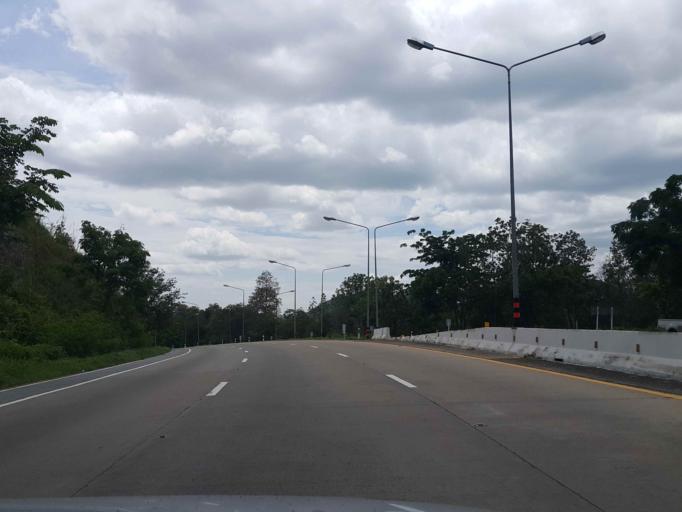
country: TH
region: Lamphun
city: Mae Tha
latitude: 18.4920
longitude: 99.1338
